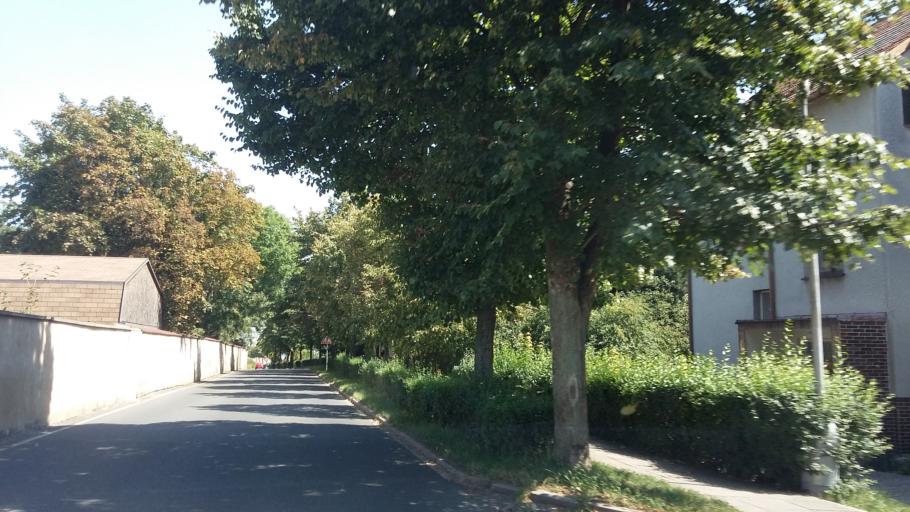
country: CZ
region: Central Bohemia
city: Zelenec
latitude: 50.1336
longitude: 14.6623
